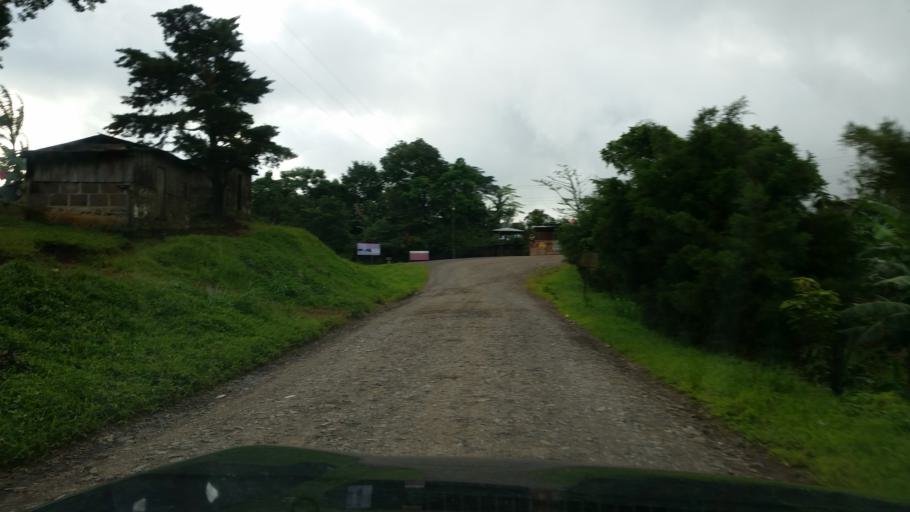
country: NI
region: Jinotega
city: San Jose de Bocay
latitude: 13.2791
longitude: -85.7264
